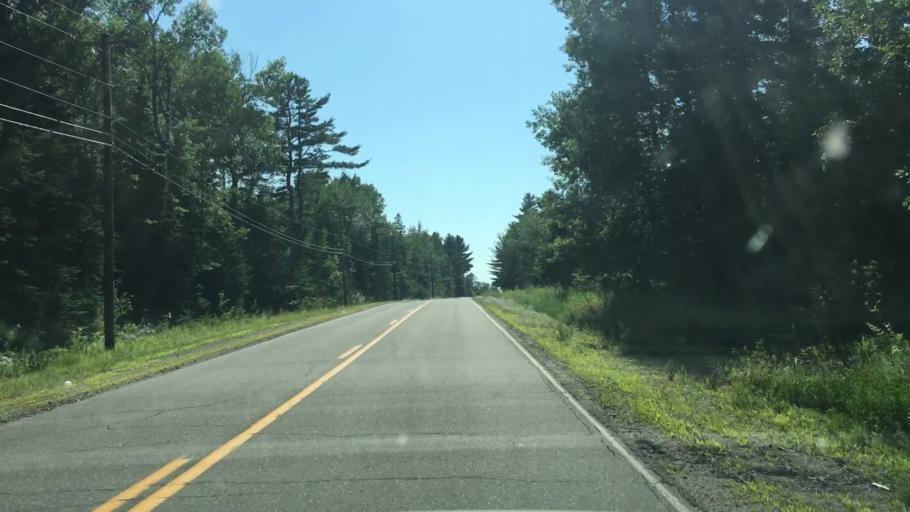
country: US
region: Maine
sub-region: Penobscot County
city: Howland
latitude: 45.2436
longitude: -68.6164
